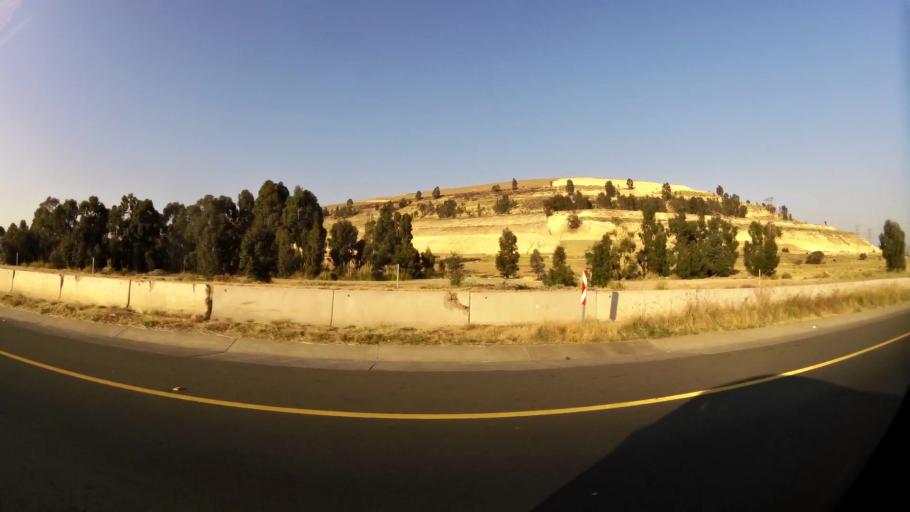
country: ZA
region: Gauteng
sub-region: City of Johannesburg Metropolitan Municipality
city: Johannesburg
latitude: -26.2172
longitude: 27.9547
